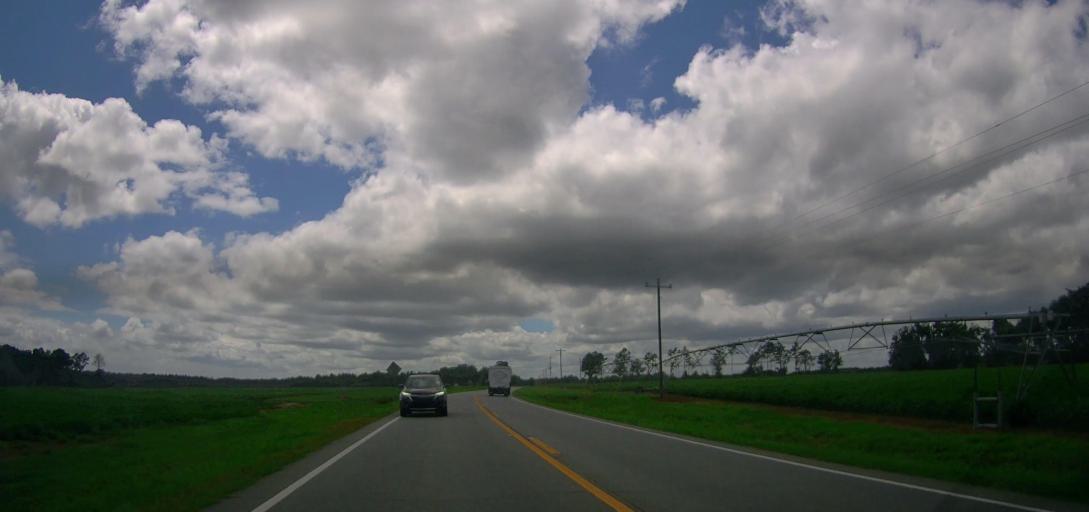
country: US
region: Georgia
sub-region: Irwin County
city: Ocilla
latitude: 31.6458
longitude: -83.3385
